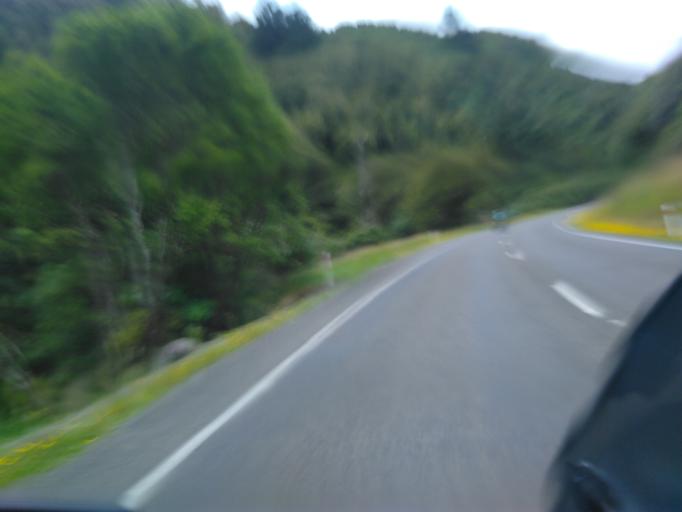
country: NZ
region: Bay of Plenty
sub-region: Opotiki District
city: Opotiki
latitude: -38.3406
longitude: 177.4326
